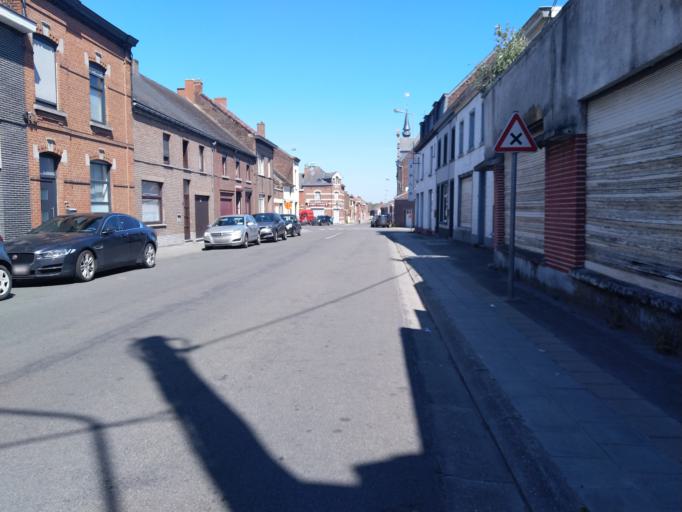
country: BE
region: Wallonia
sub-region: Province du Hainaut
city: Colfontaine
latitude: 50.4073
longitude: 3.8629
